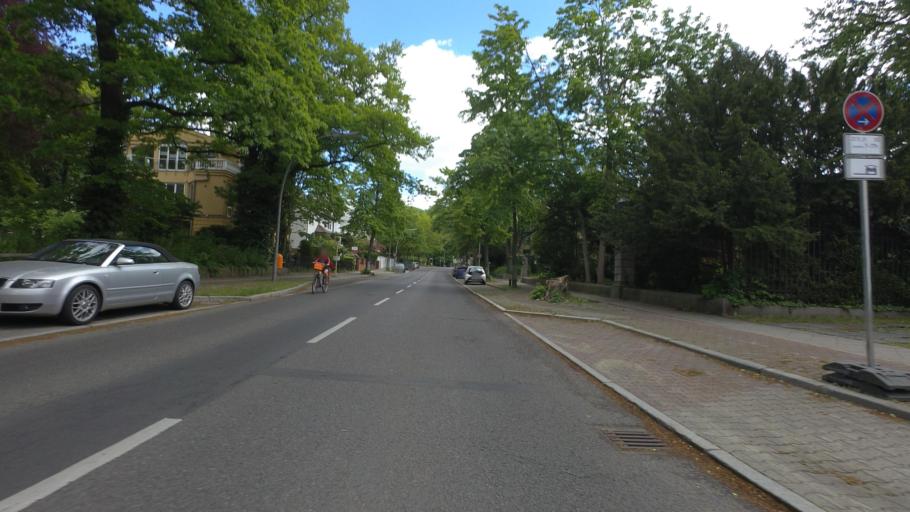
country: DE
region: Berlin
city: Grunewald
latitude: 52.4894
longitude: 13.2754
